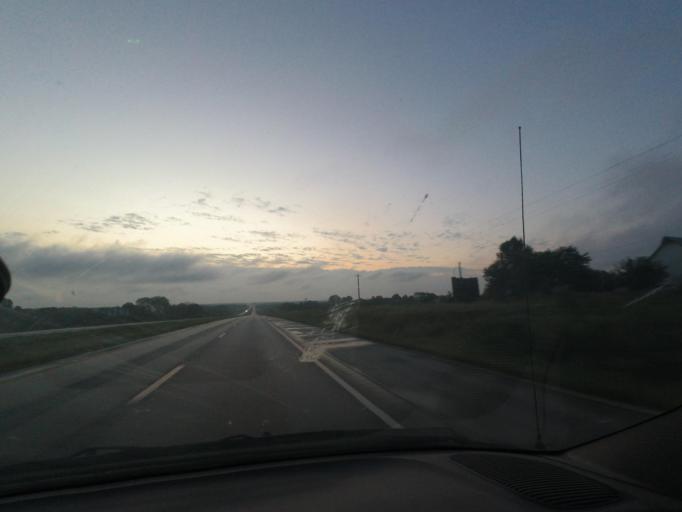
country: US
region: Missouri
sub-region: Linn County
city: Brookfield
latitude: 39.7622
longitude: -93.0072
